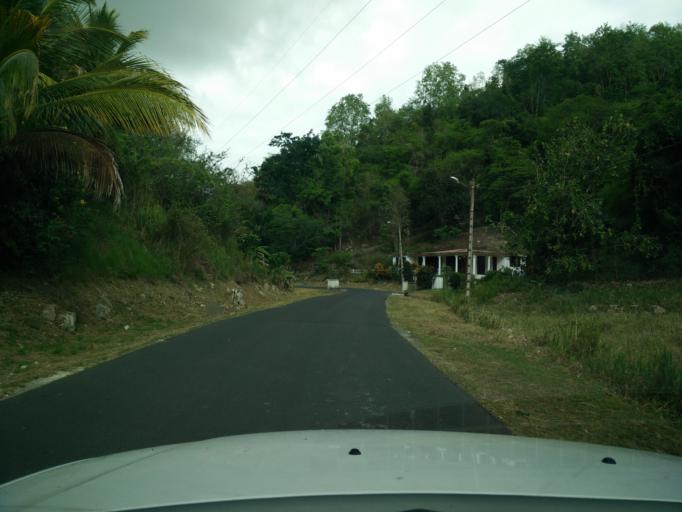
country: GP
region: Guadeloupe
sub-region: Guadeloupe
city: Le Gosier
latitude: 16.2236
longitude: -61.4664
